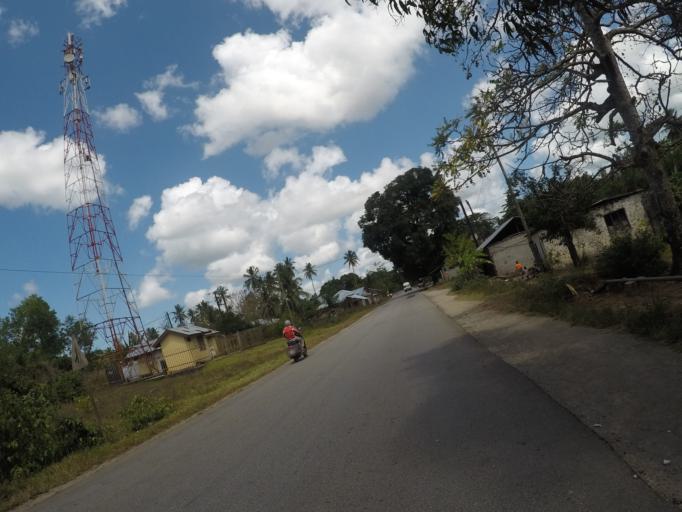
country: TZ
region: Zanzibar Central/South
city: Nganane
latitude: -6.2875
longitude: 39.4376
